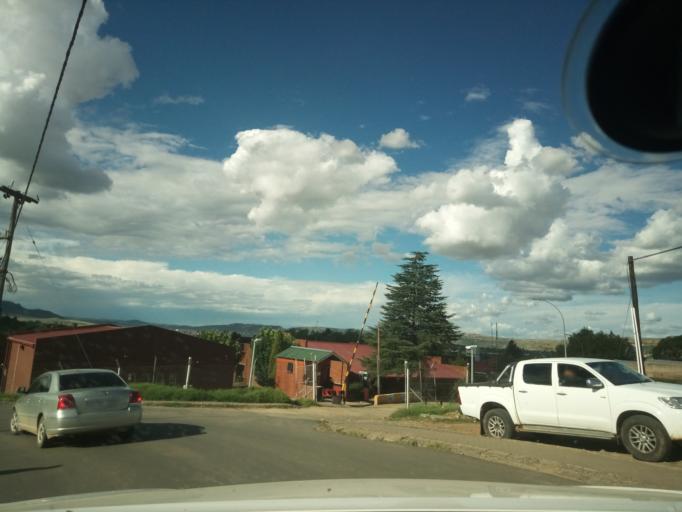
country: LS
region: Maseru
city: Maseru
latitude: -29.3269
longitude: 27.5008
